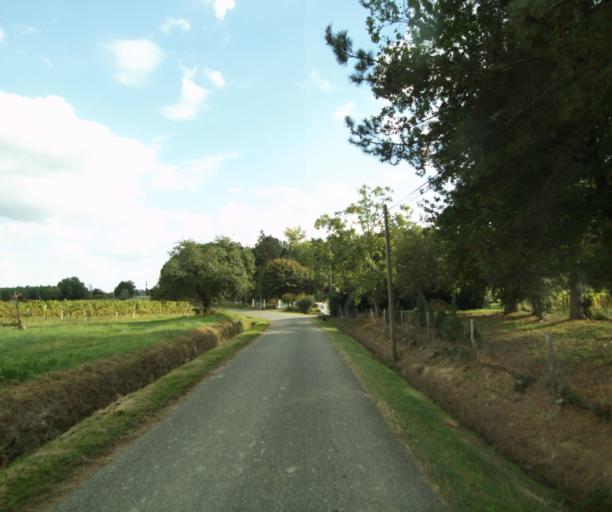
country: FR
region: Midi-Pyrenees
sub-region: Departement du Gers
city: Cazaubon
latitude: 43.8956
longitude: -0.0479
